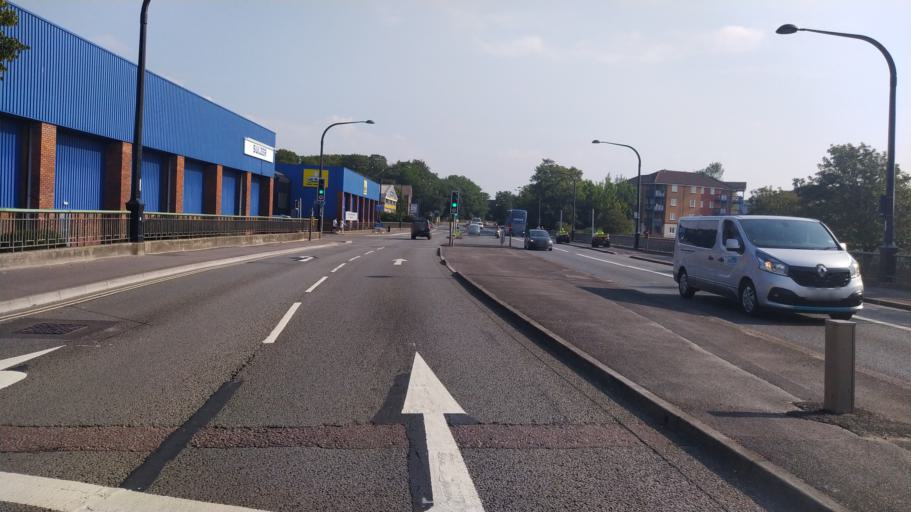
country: GB
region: England
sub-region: Southampton
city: Southampton
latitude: 50.9156
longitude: -1.3852
